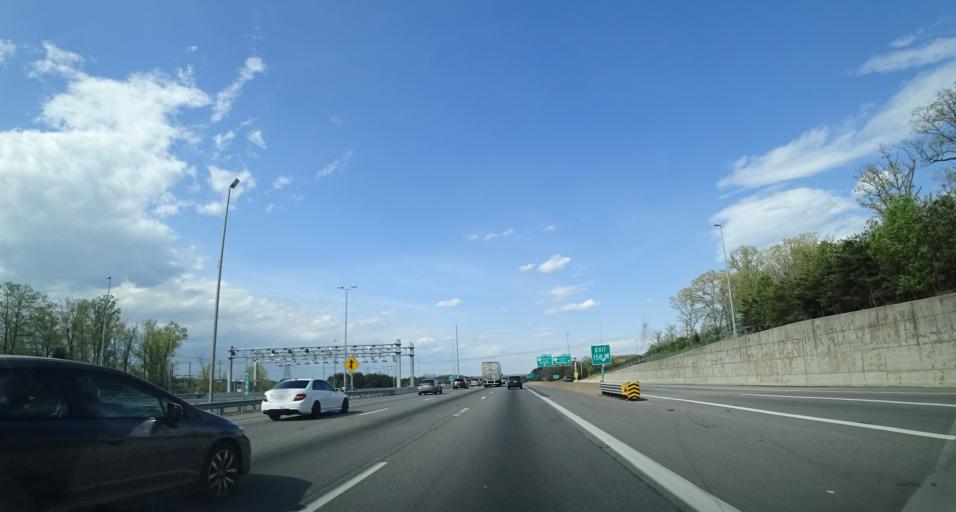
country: US
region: Virginia
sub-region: Prince William County
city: Potomac Mills
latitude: 38.6523
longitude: -77.2816
